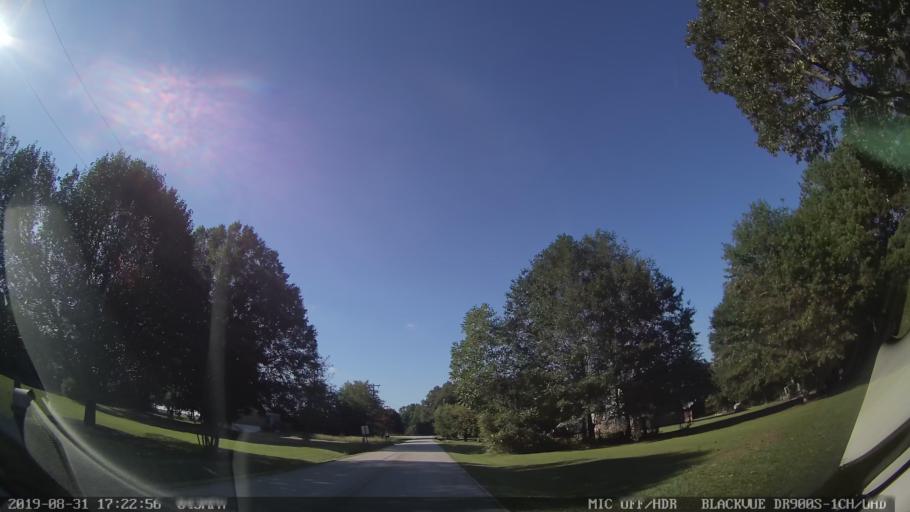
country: US
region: South Carolina
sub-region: Spartanburg County
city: Boiling Springs
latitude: 35.0807
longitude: -81.9384
